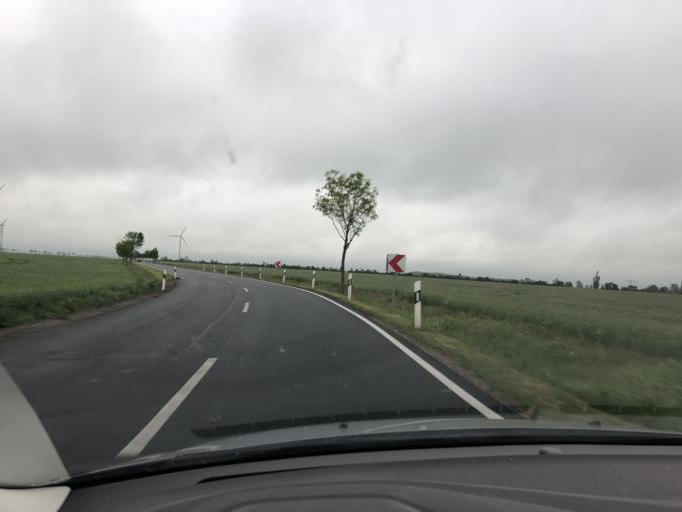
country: DE
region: Saxony
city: Dobernitz
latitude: 51.5100
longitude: 12.3738
